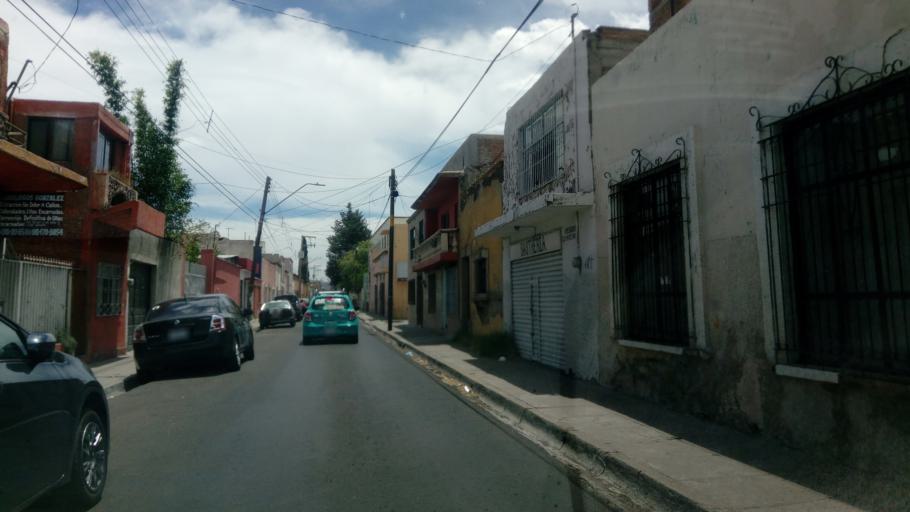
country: MX
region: Durango
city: Victoria de Durango
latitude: 24.0185
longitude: -104.6685
